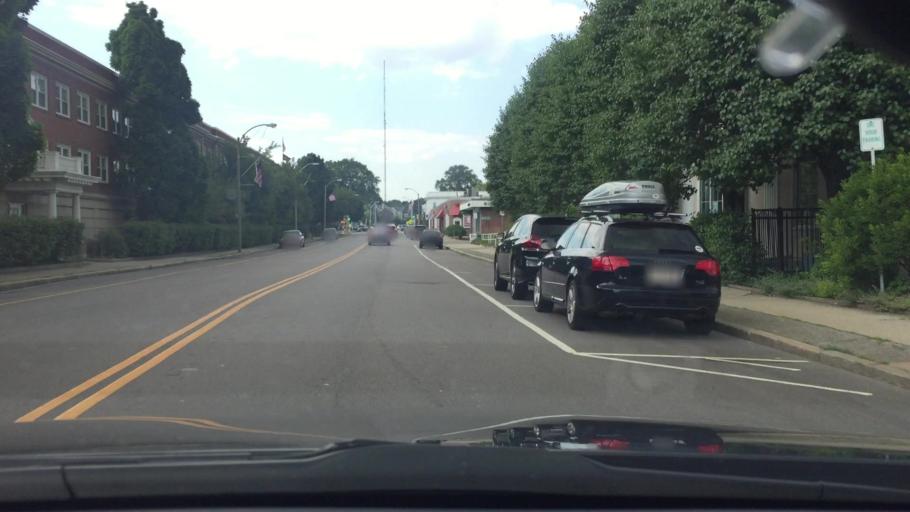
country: US
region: Massachusetts
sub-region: Norfolk County
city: Needham
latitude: 42.2913
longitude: -71.2351
